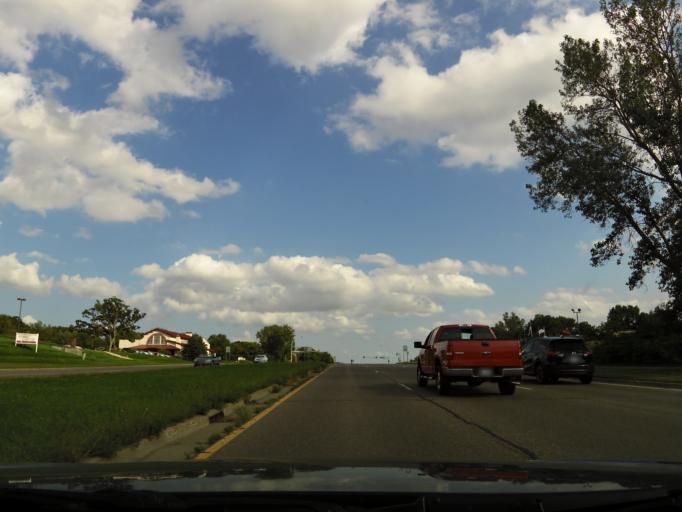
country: US
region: Minnesota
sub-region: Dakota County
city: Burnsville
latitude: 44.7424
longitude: -93.2752
